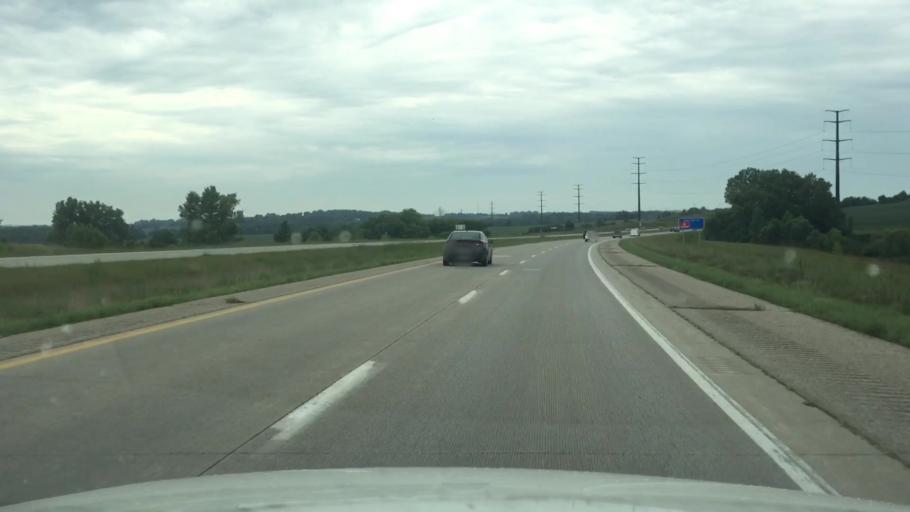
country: US
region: Iowa
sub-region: Warren County
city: Norwalk
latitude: 41.4981
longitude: -93.6026
